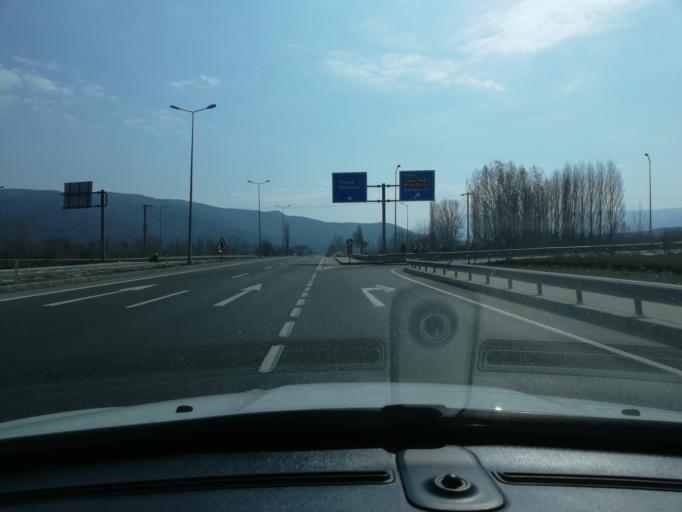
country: TR
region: Cankiri
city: Ilgaz
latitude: 40.9050
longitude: 33.6511
